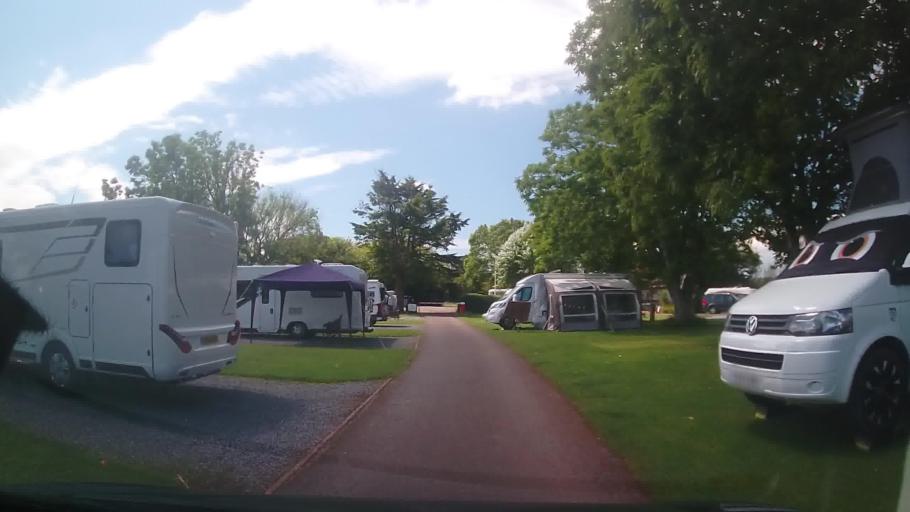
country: GB
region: England
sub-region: Devon
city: Dartmouth
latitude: 50.2927
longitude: -3.6495
